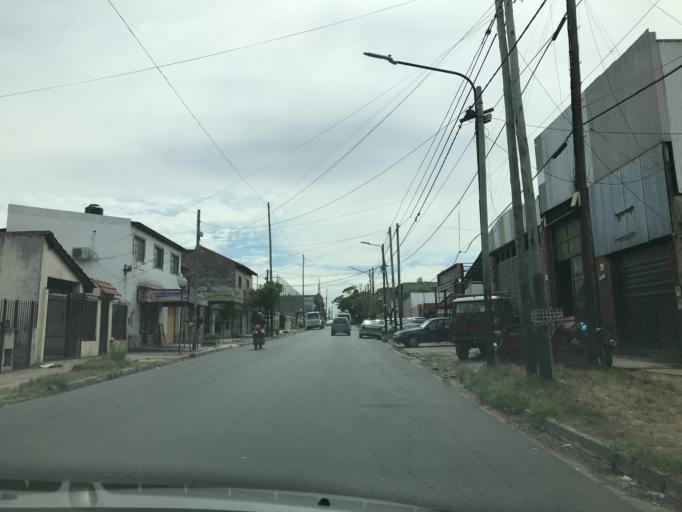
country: AR
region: Buenos Aires
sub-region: Partido de Lomas de Zamora
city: Lomas de Zamora
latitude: -34.7318
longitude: -58.4269
